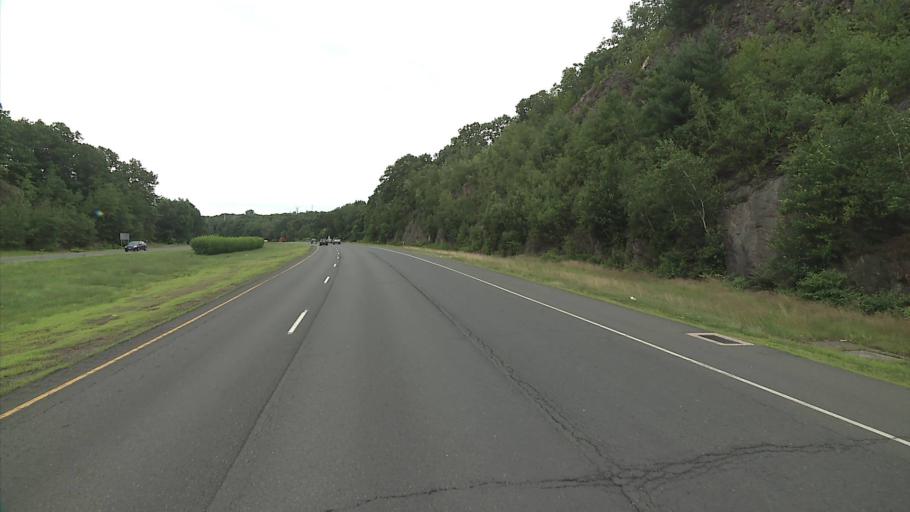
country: US
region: Connecticut
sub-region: Litchfield County
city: Oakville
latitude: 41.6007
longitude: -73.0667
